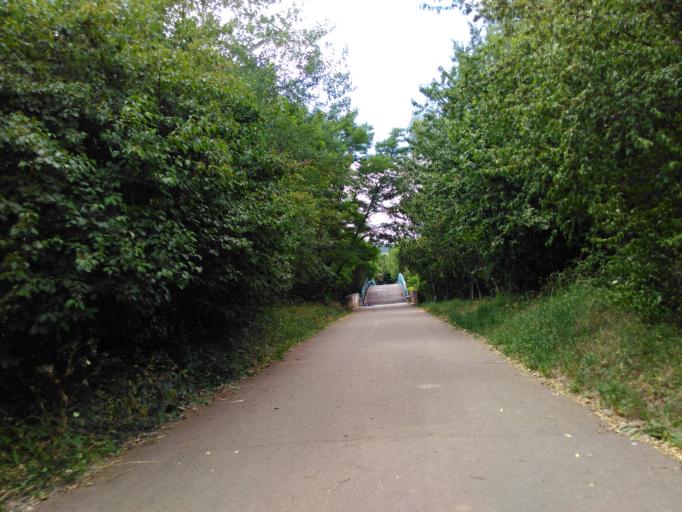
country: LU
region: Luxembourg
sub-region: Canton d'Esch-sur-Alzette
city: Petange
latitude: 49.5611
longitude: 5.8839
